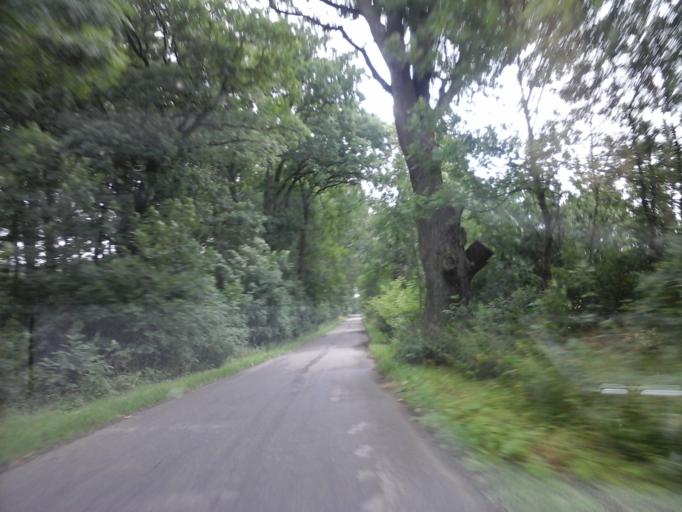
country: PL
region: West Pomeranian Voivodeship
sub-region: Powiat choszczenski
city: Krzecin
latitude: 52.9886
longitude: 15.5212
